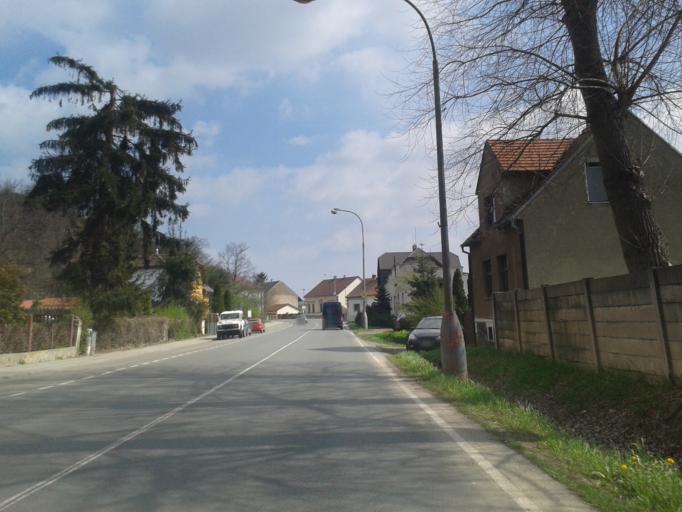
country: CZ
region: Central Bohemia
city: Zdice
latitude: 49.9081
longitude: 13.9721
